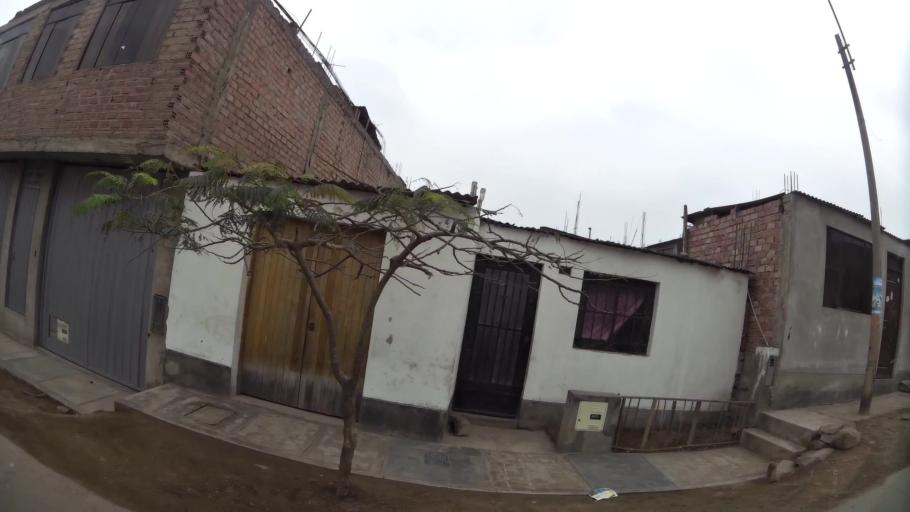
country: PE
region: Lima
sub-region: Lima
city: Surco
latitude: -12.1793
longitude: -76.9595
